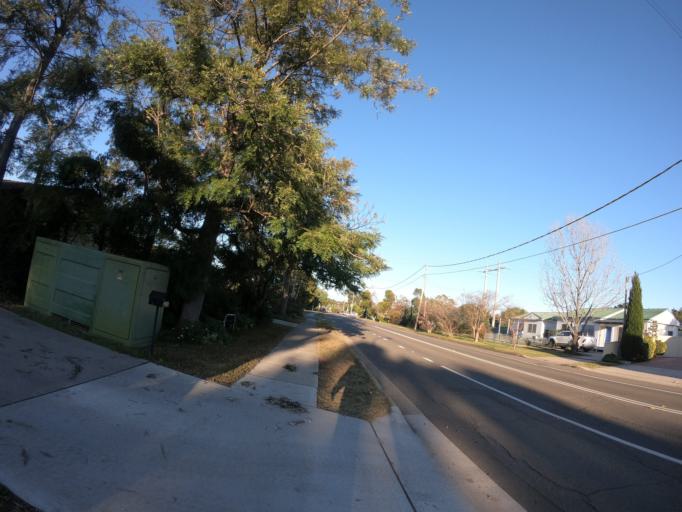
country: AU
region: New South Wales
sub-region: Hawkesbury
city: South Windsor
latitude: -33.6263
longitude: 150.8012
